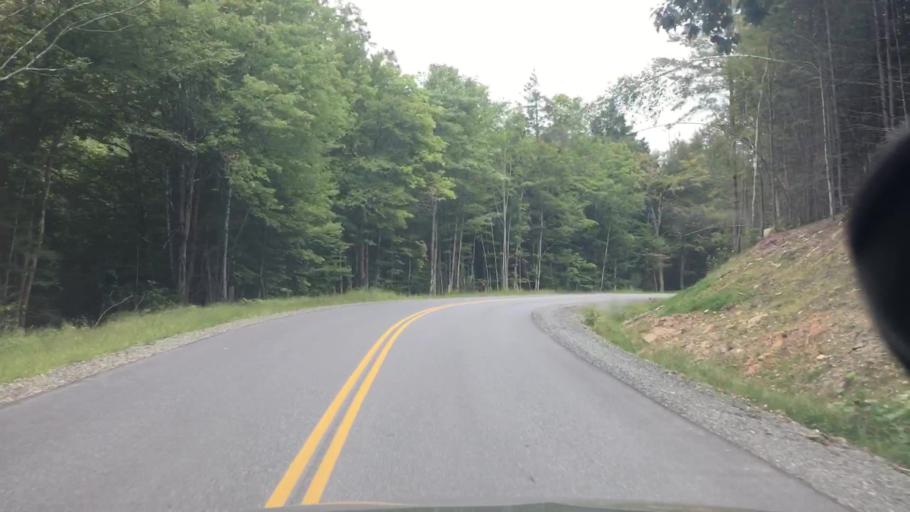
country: US
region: Massachusetts
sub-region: Franklin County
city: Colrain
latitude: 42.7742
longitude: -72.7675
